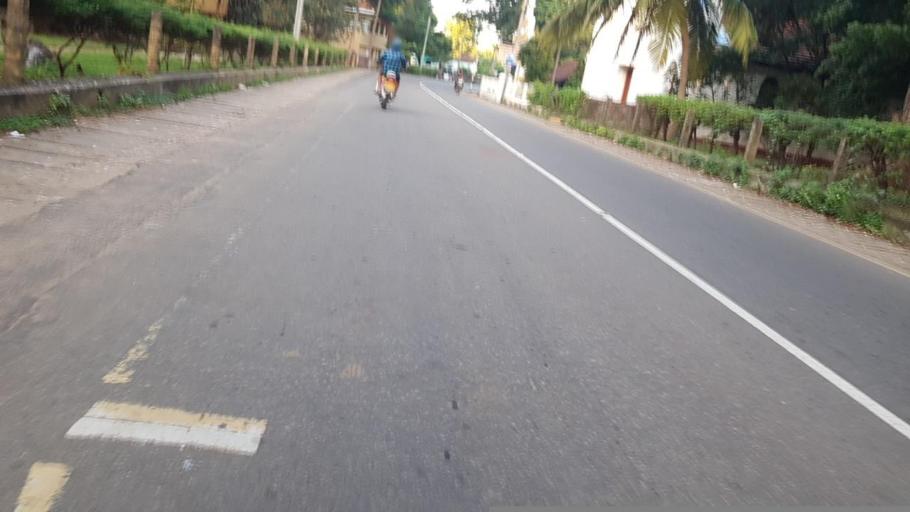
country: LK
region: Northern Province
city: Jaffna
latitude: 9.7290
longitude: 79.9488
